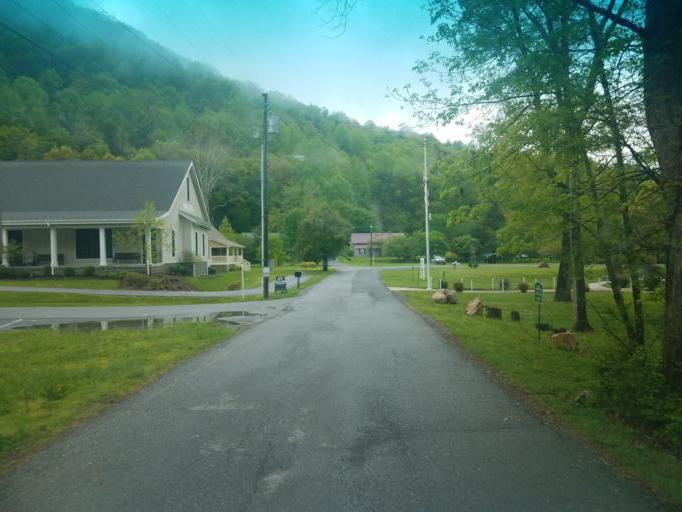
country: US
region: Virginia
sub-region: Washington County
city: Emory
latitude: 36.6315
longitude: -81.7903
